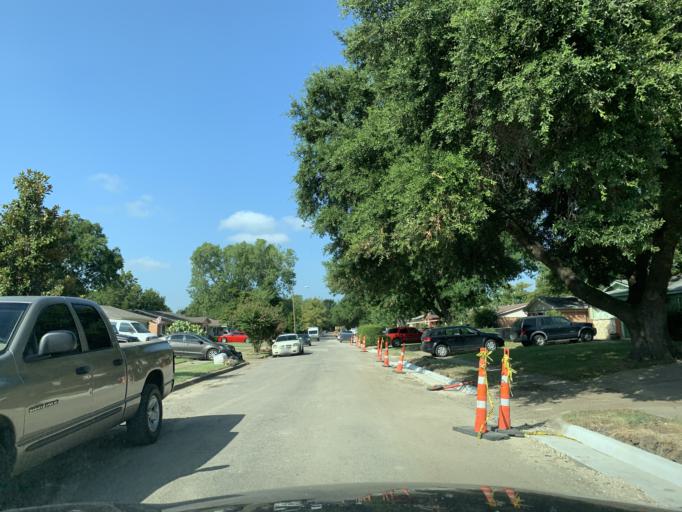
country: US
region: Texas
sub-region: Dallas County
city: Hutchins
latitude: 32.6925
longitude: -96.7866
